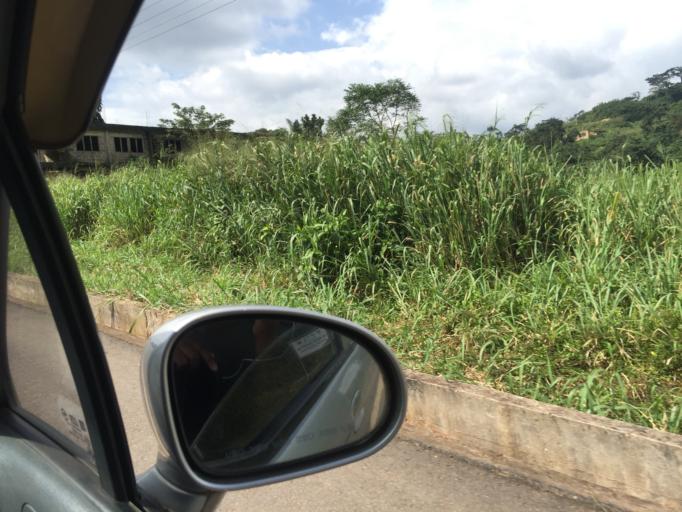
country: GH
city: Mpraeso
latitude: 6.5769
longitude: -0.7296
